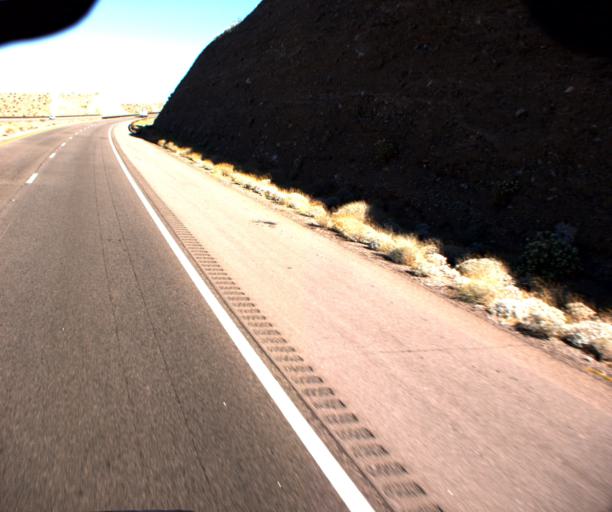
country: US
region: Nevada
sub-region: Clark County
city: Boulder City
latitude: 35.8927
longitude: -114.6240
